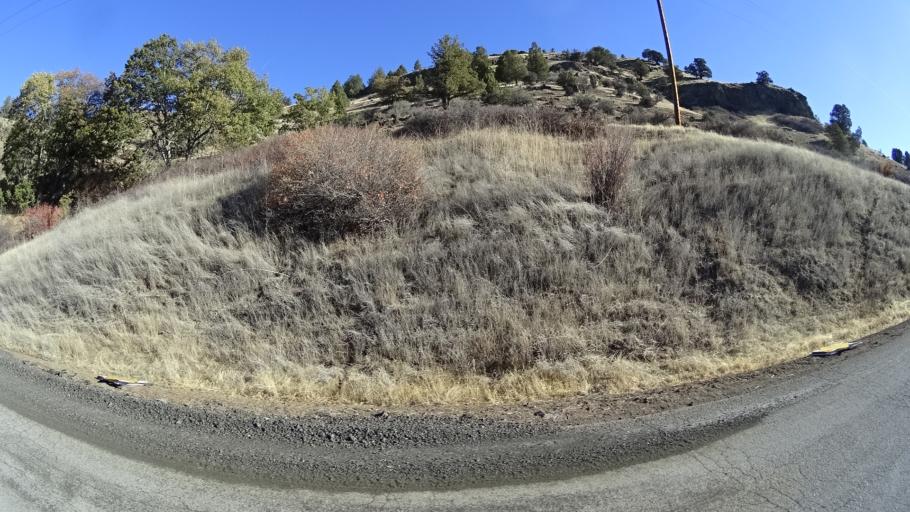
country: US
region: California
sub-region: Siskiyou County
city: Montague
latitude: 41.9706
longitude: -122.3961
